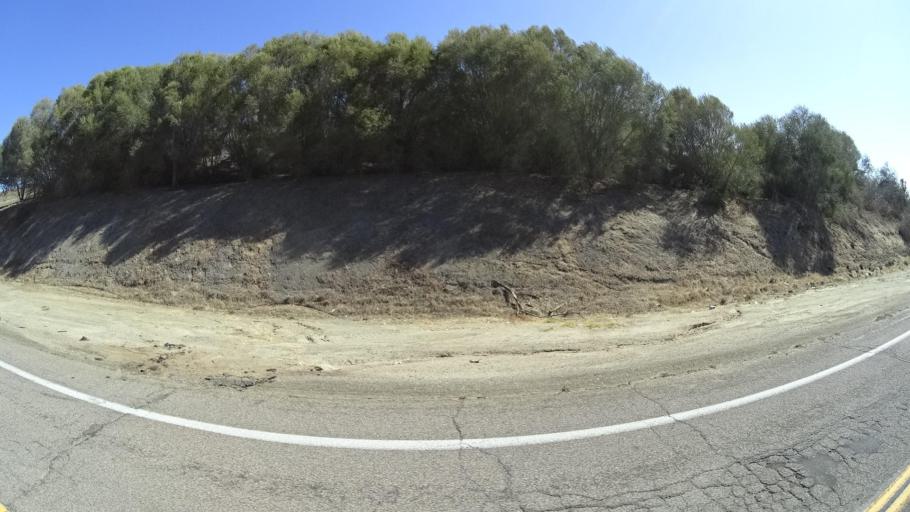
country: US
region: California
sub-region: San Diego County
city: Hidden Meadows
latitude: 33.2677
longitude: -117.1265
